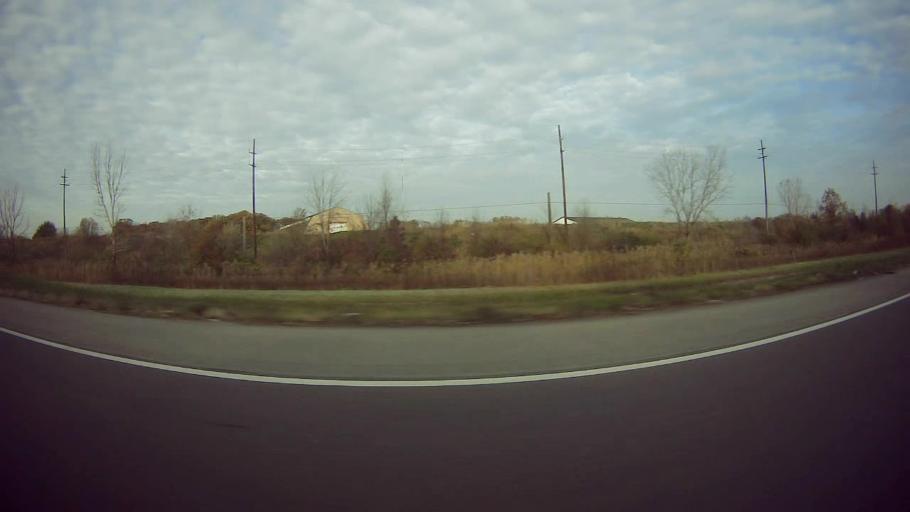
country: US
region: Michigan
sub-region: Macomb County
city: Mount Clemens
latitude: 42.5511
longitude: -82.8769
